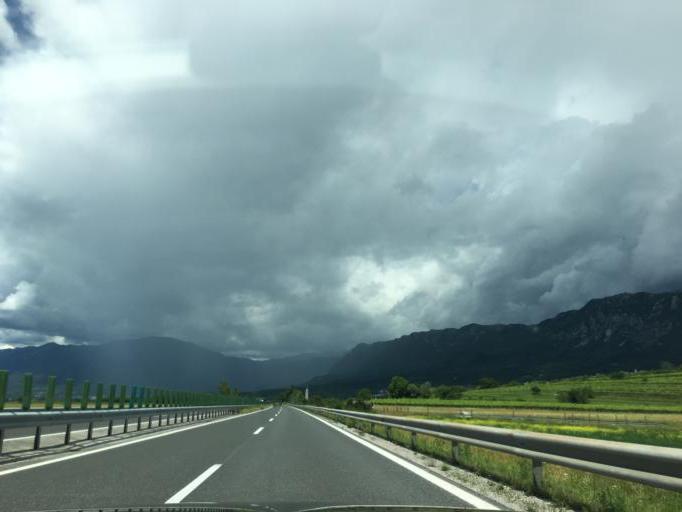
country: SI
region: Vipava
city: Vipava
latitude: 45.8512
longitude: 13.9467
